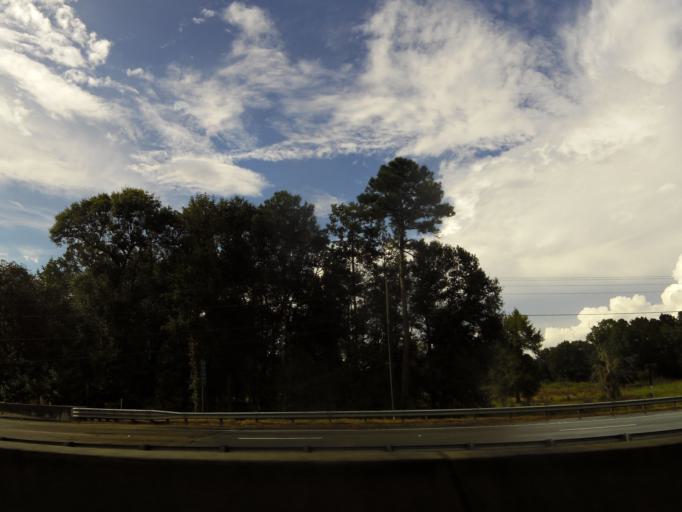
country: US
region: Georgia
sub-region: Long County
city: Ludowici
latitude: 31.7353
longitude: -81.7044
